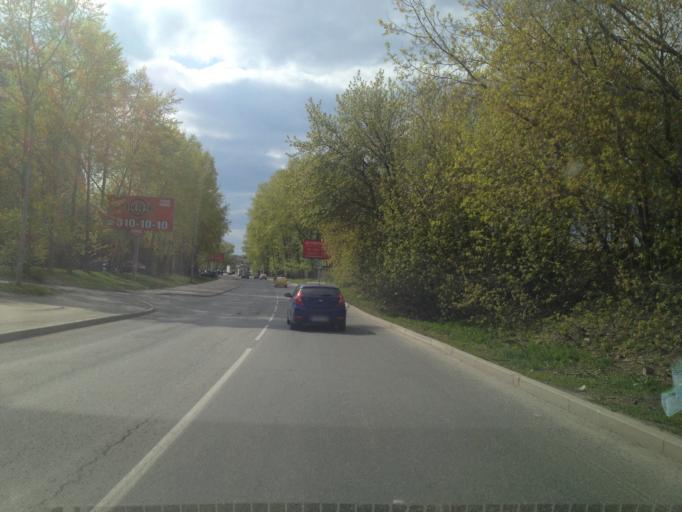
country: RU
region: Sverdlovsk
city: Yekaterinburg
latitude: 56.8570
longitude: 60.5713
